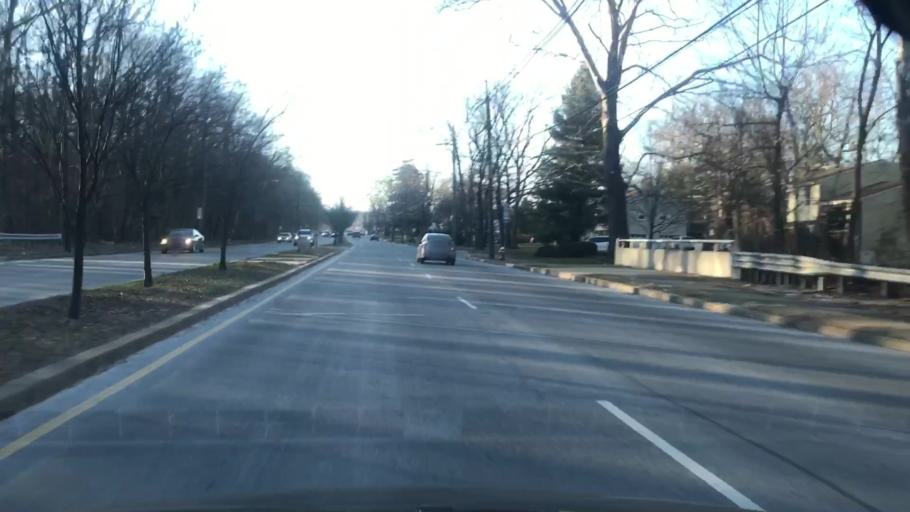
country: US
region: New Jersey
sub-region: Essex County
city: Northfield
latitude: 40.7725
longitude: -74.3148
